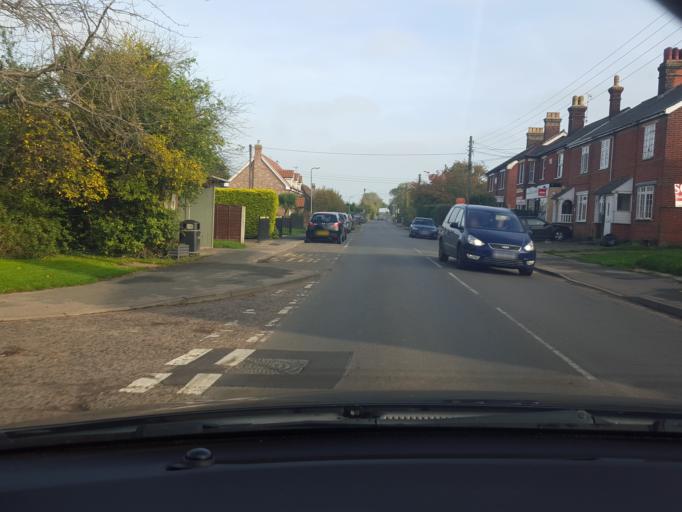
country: GB
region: England
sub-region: Essex
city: Frinton-on-Sea
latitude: 51.8517
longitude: 1.2308
